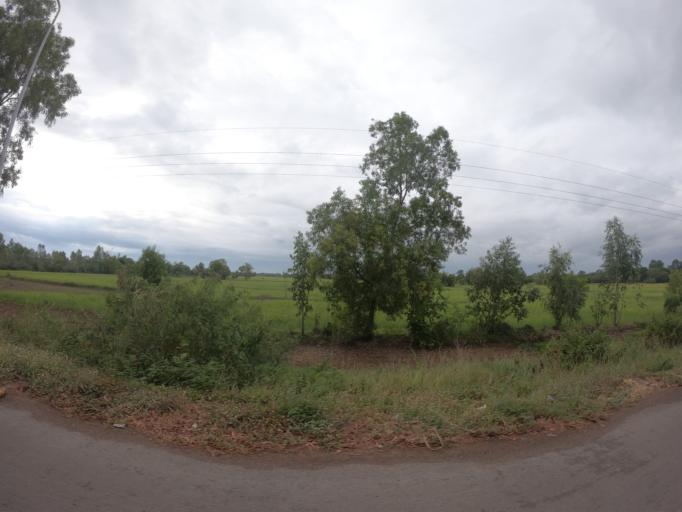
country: TH
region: Roi Et
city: Thawat Buri
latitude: 16.0850
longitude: 103.7494
